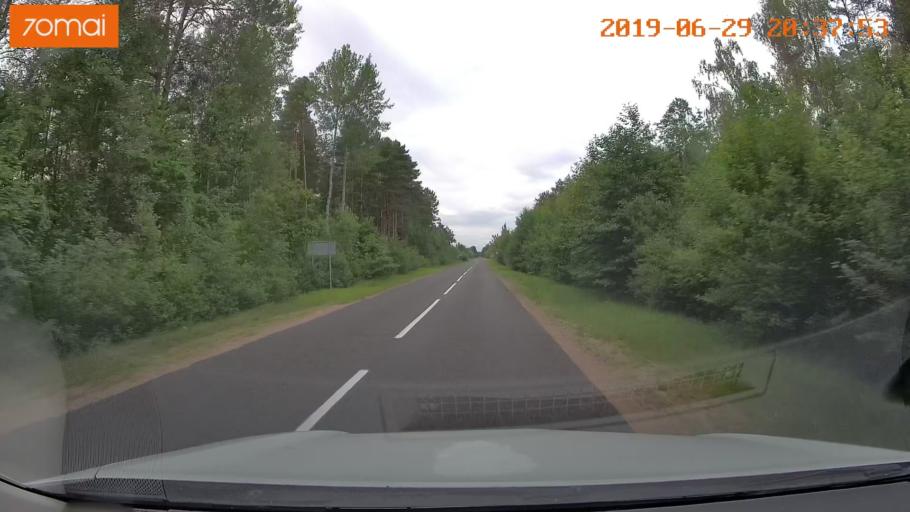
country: BY
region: Brest
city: Hantsavichy
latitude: 52.5433
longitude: 26.3657
